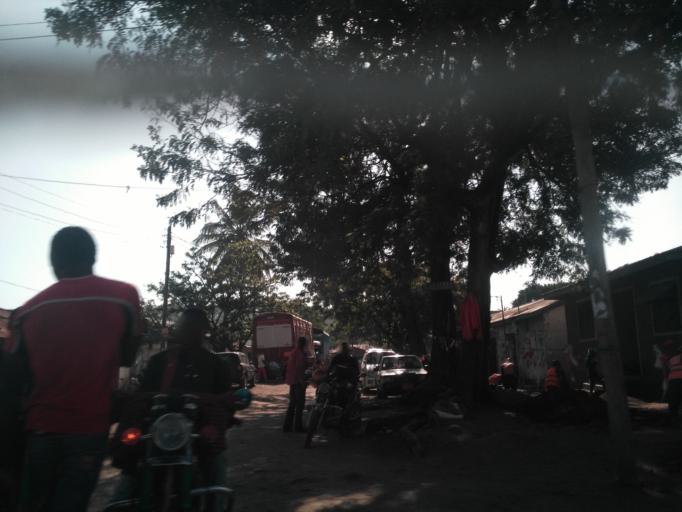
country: TZ
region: Mwanza
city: Mwanza
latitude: -2.5055
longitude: 32.8964
